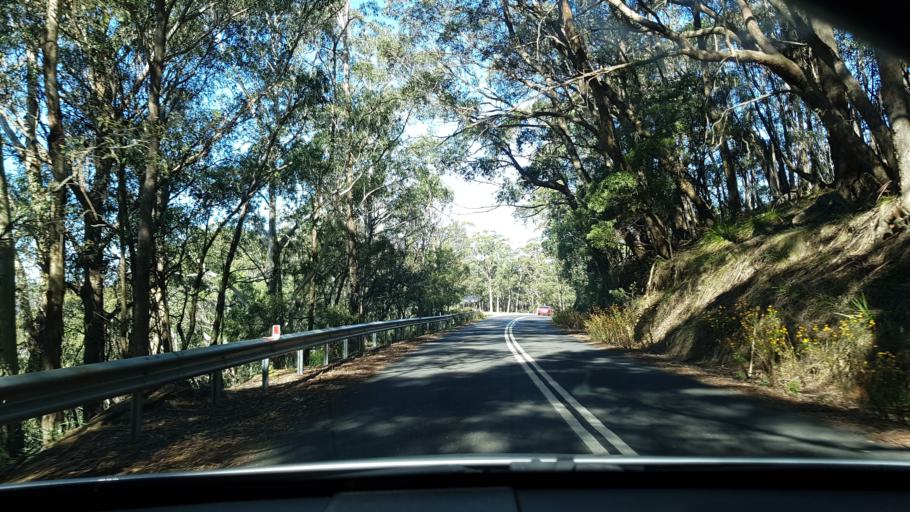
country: AU
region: New South Wales
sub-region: Oberon
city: Oberon
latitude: -33.7896
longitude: 150.0302
